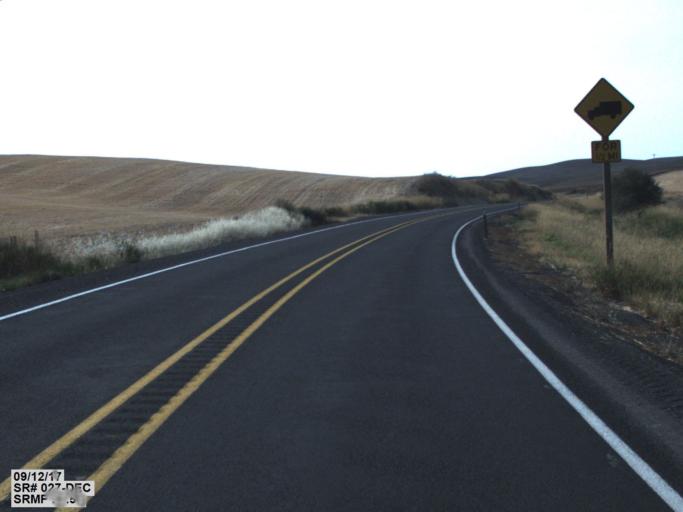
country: US
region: Washington
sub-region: Whitman County
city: Colfax
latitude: 47.0006
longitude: -117.1319
